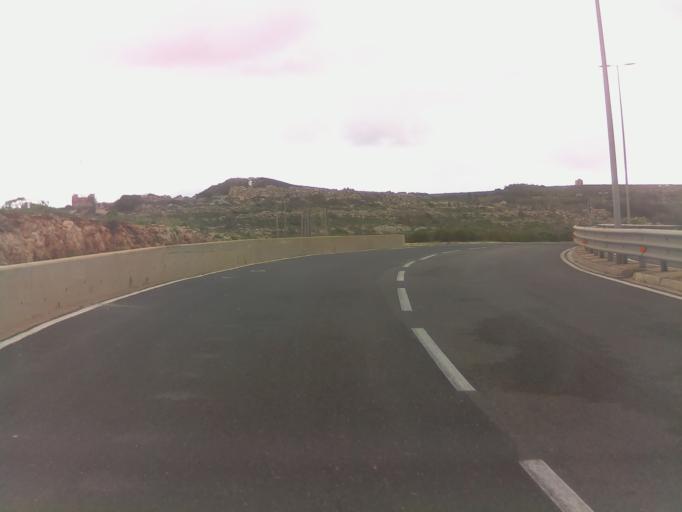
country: MT
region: Il-Mellieha
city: Mellieha
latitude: 35.9839
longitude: 14.3420
